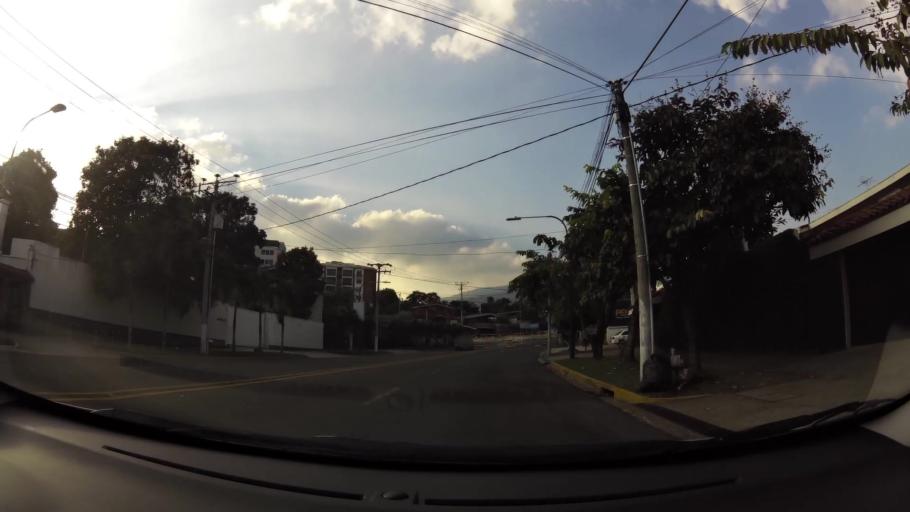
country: SV
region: La Libertad
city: Antiguo Cuscatlan
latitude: 13.6895
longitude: -89.2432
